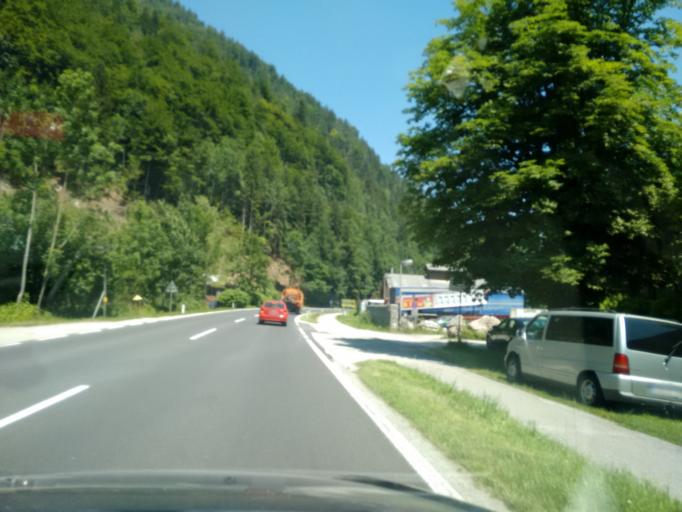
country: AT
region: Upper Austria
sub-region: Politischer Bezirk Gmunden
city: Bad Ischl
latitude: 47.7254
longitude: 13.6466
